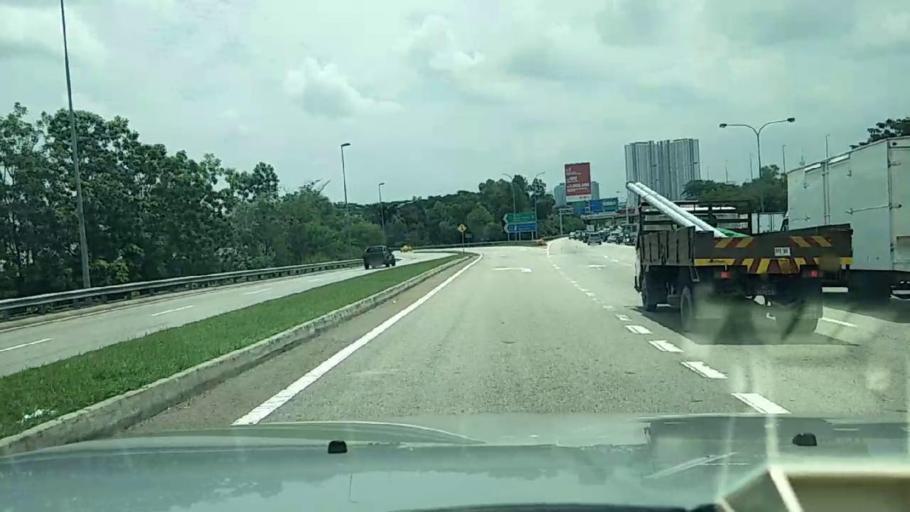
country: MY
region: Kuala Lumpur
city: Kuala Lumpur
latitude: 3.0915
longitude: 101.6954
